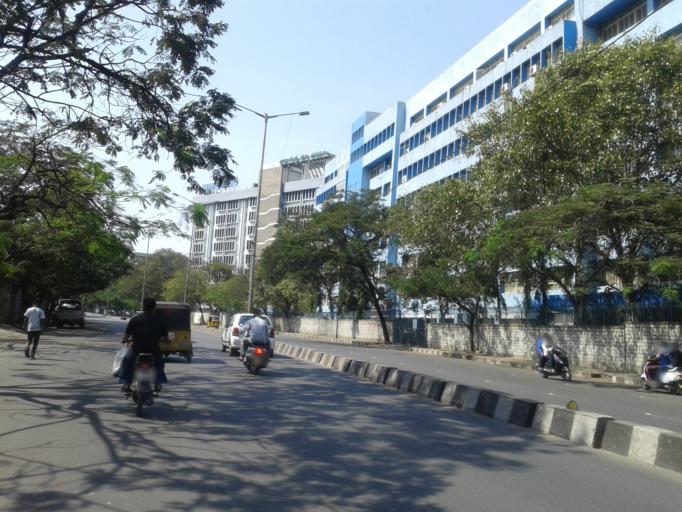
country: IN
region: Telangana
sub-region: Hyderabad
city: Hyderabad
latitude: 17.4012
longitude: 78.4744
